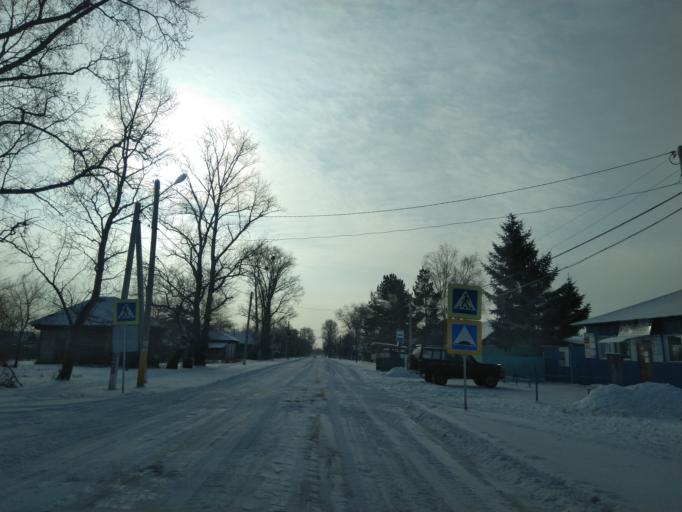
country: RU
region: Amur
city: Poyarkovo
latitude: 49.6284
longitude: 128.6498
